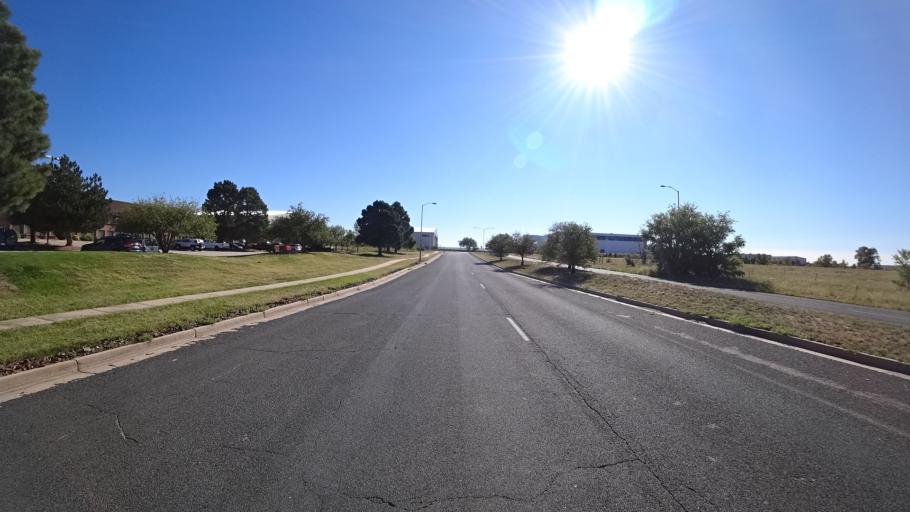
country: US
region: Colorado
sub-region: El Paso County
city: Cimarron Hills
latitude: 38.8062
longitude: -104.7258
